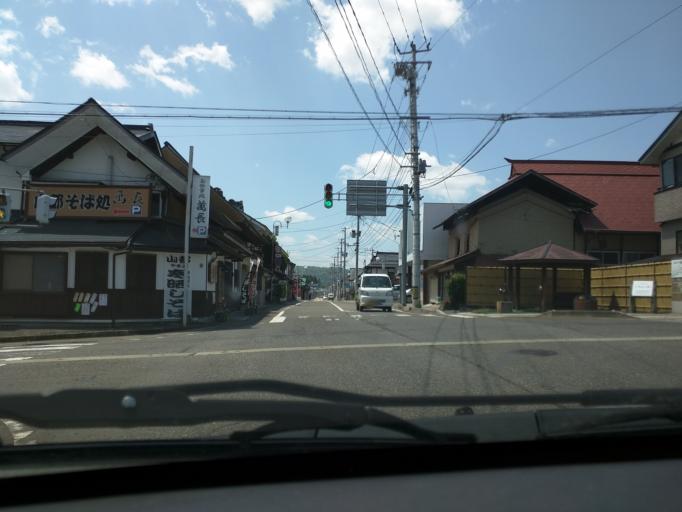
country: JP
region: Fukushima
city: Kitakata
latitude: 37.6430
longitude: 139.7737
